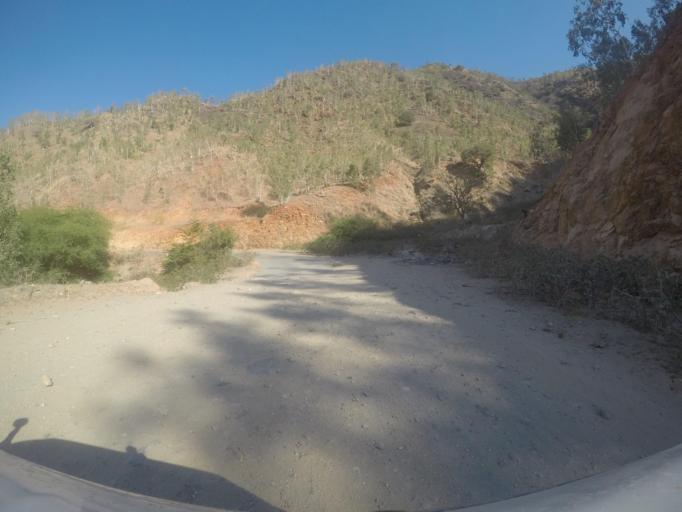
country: TL
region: Dili
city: Dili
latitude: -8.5293
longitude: 125.6248
